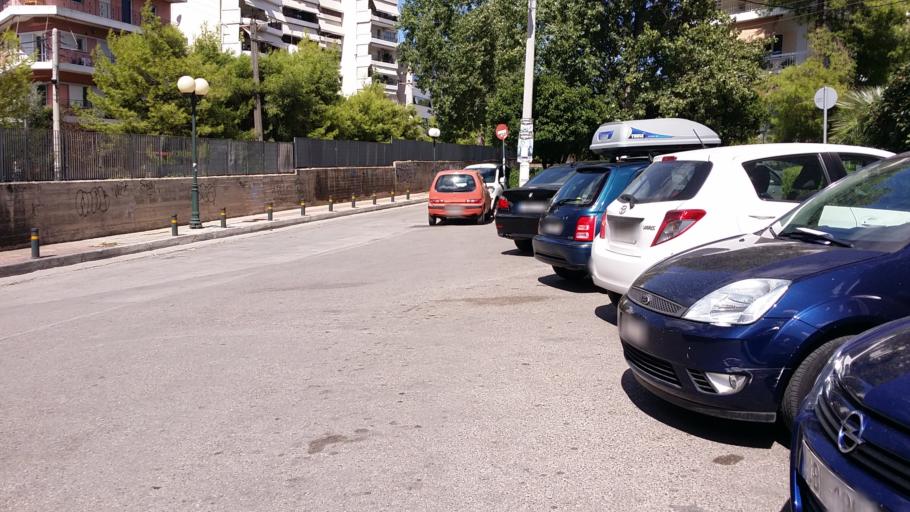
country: GR
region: Attica
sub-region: Nomarchia Athinas
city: Nea Ionia
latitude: 38.0440
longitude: 23.7598
